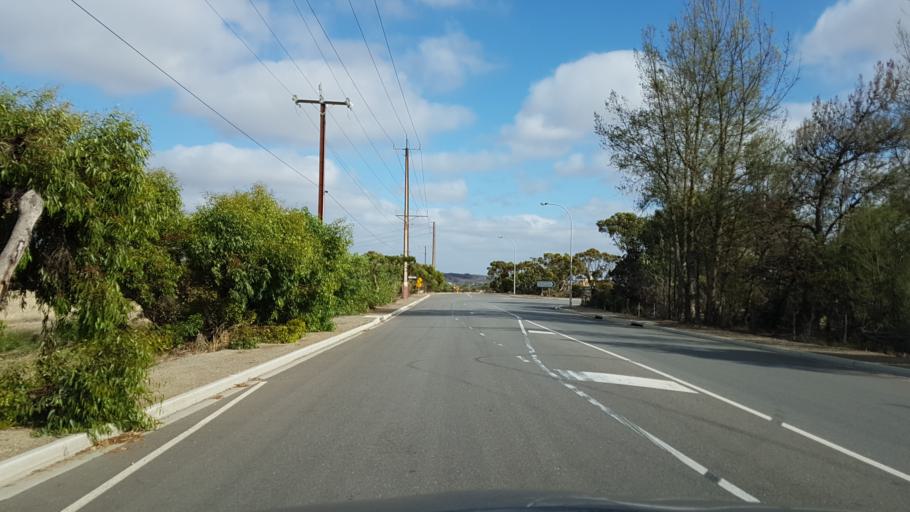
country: AU
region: South Australia
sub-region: Murray Bridge
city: Murray Bridge
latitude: -35.1177
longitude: 139.2476
